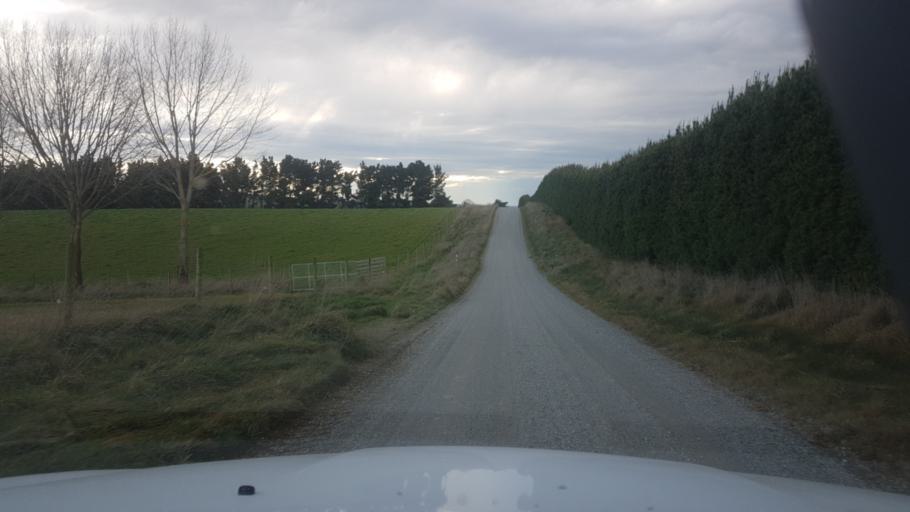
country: NZ
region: Canterbury
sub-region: Timaru District
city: Pleasant Point
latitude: -44.3420
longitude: 171.1415
